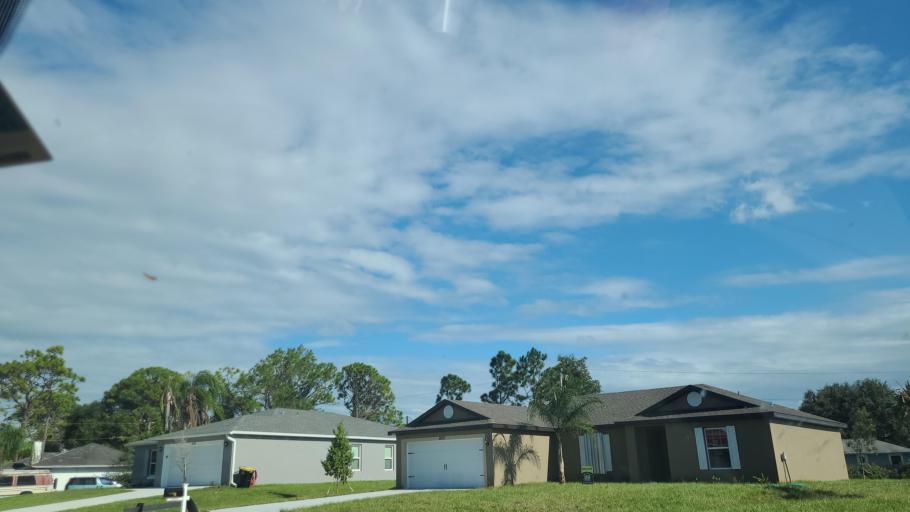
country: US
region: Florida
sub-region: Brevard County
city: Grant-Valkaria
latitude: 27.9603
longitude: -80.6254
